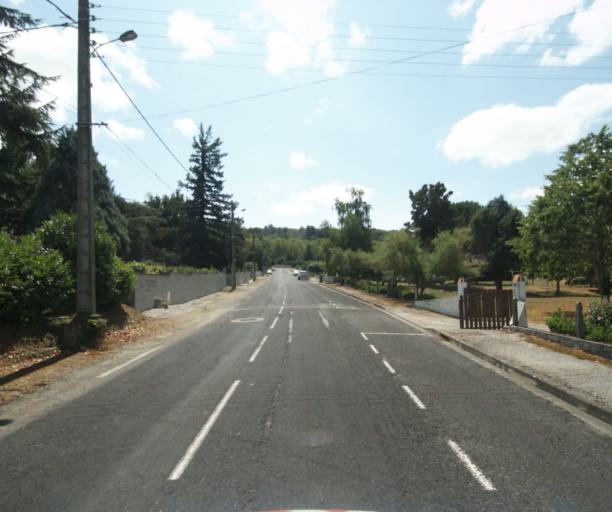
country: FR
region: Midi-Pyrenees
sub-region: Departement de la Haute-Garonne
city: Revel
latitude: 43.4495
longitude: 2.0093
